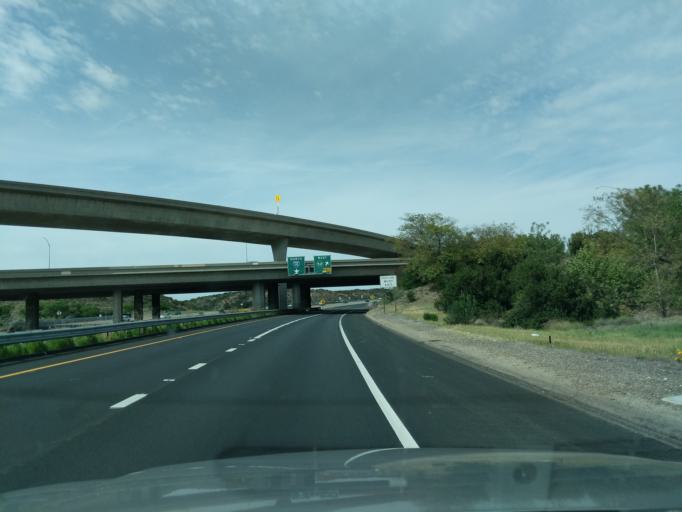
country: US
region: California
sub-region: San Diego County
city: La Mesa
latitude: 32.8409
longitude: -117.1203
